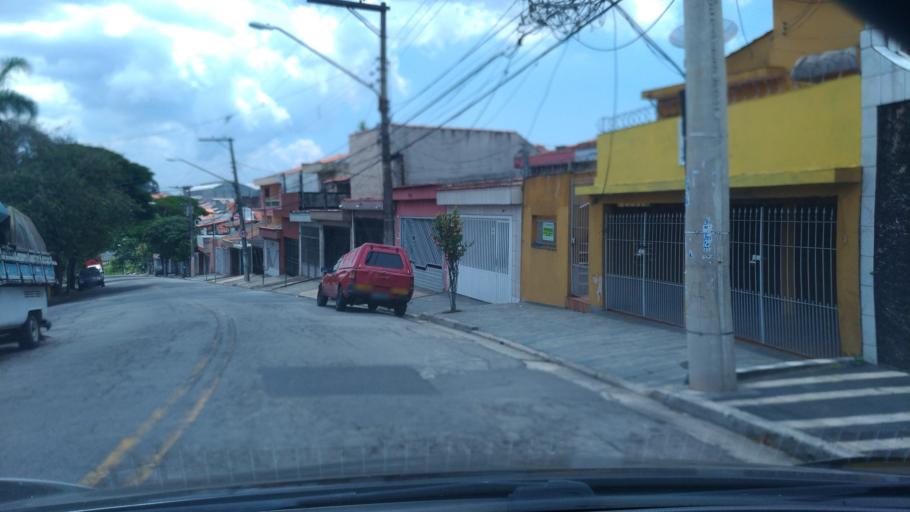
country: BR
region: Sao Paulo
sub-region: Sao Bernardo Do Campo
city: Sao Bernardo do Campo
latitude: -23.7055
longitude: -46.5841
